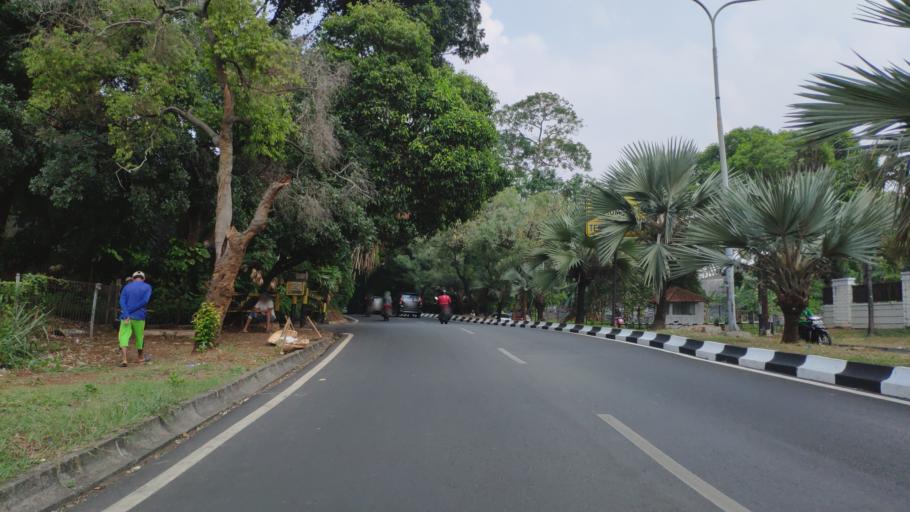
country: ID
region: Banten
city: South Tangerang
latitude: -6.2831
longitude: 106.7861
